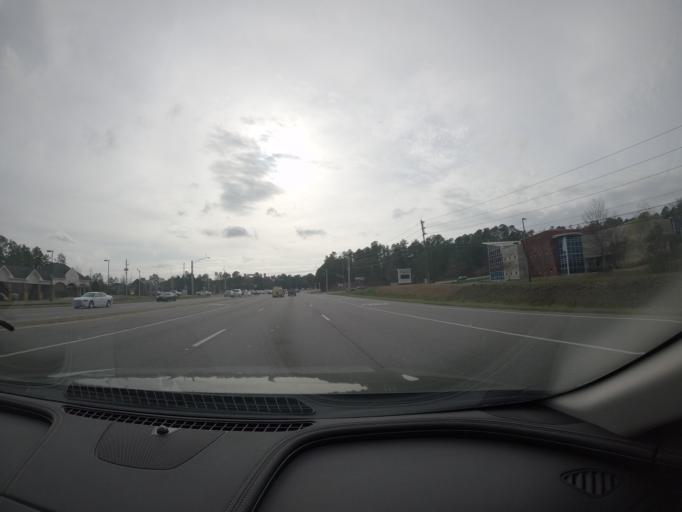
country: US
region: Georgia
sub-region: Columbia County
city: Martinez
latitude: 33.5234
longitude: -82.0478
